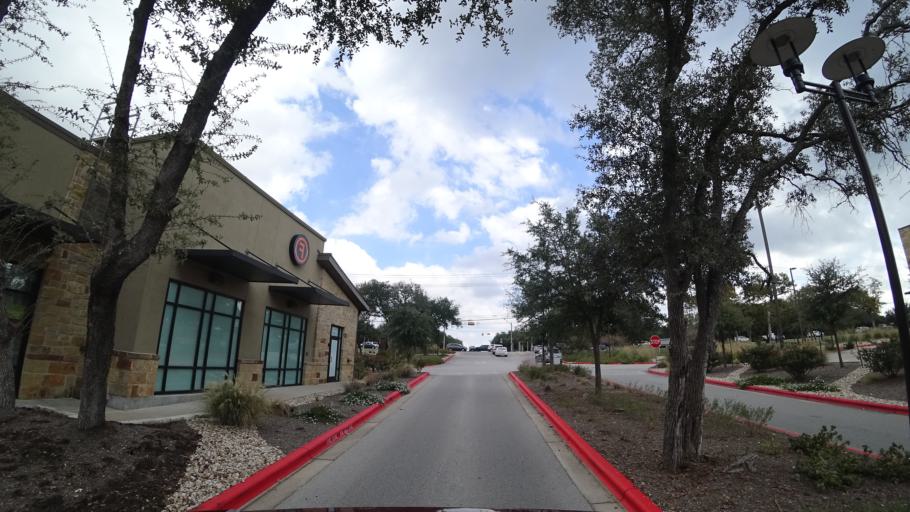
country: US
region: Texas
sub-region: Williamson County
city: Anderson Mill
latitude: 30.4222
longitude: -97.8459
